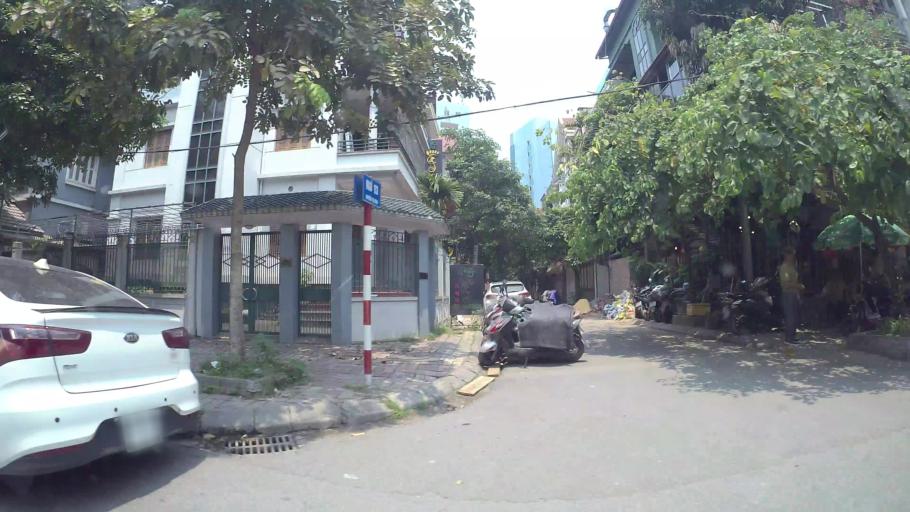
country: VN
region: Ha Noi
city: Thanh Xuan
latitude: 21.0078
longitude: 105.8052
